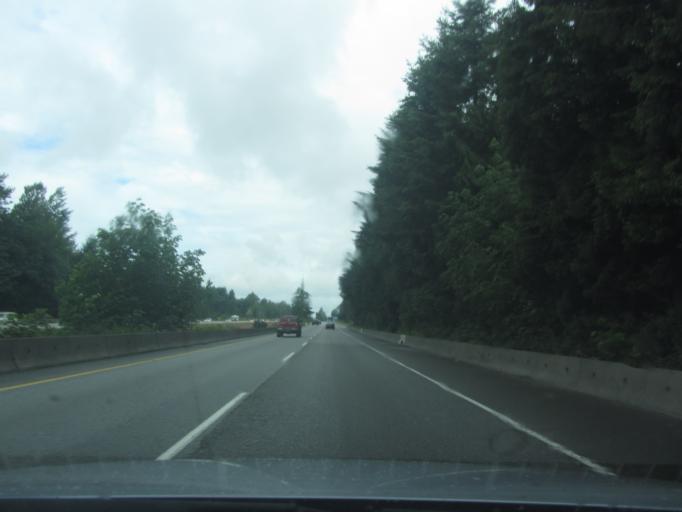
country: CA
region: British Columbia
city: Langley
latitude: 49.1225
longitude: -122.5454
